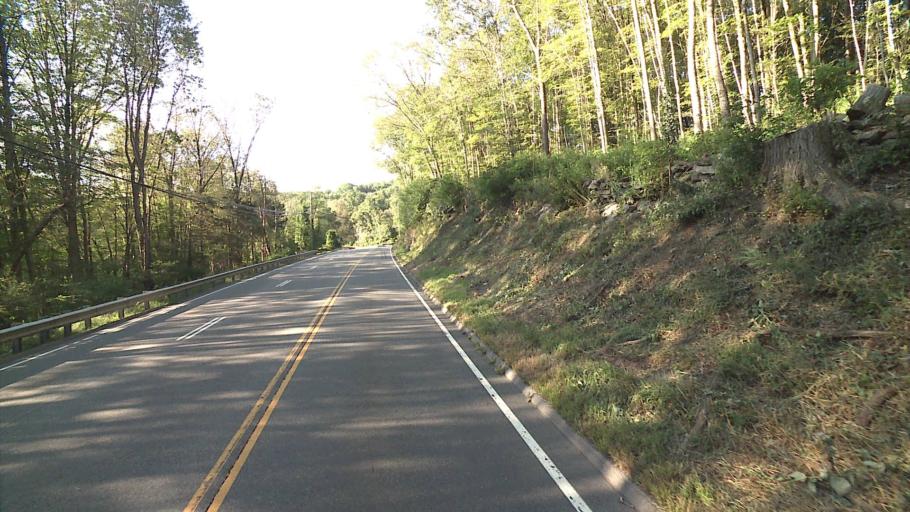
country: US
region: Connecticut
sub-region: New London County
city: Baltic
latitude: 41.6130
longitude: -72.1451
